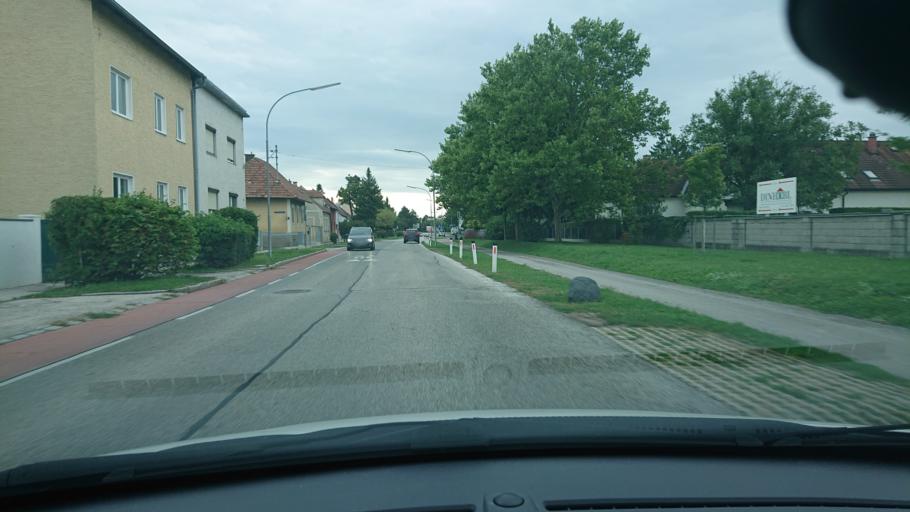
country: AT
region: Lower Austria
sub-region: Wiener Neustadt Stadt
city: Wiener Neustadt
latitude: 47.8087
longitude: 16.2201
